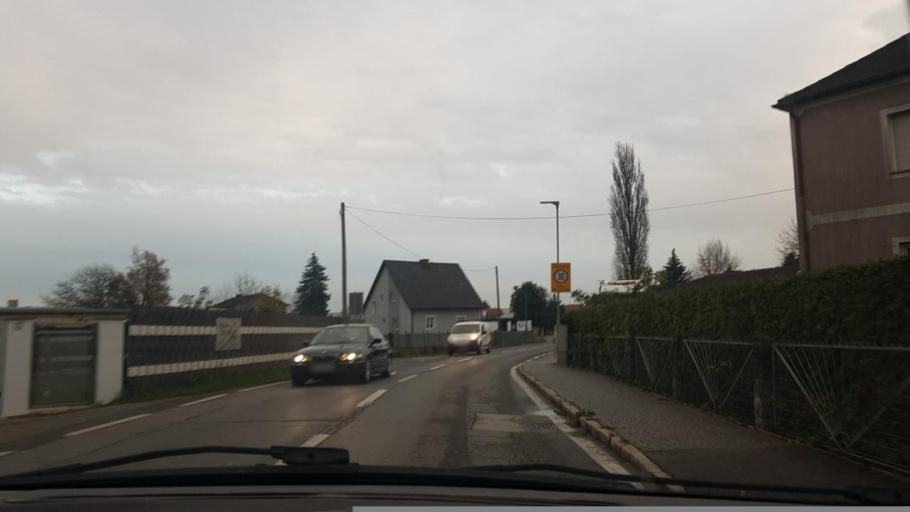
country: AT
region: Styria
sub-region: Politischer Bezirk Graz-Umgebung
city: Feldkirchen bei Graz
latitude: 47.0136
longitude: 15.4277
